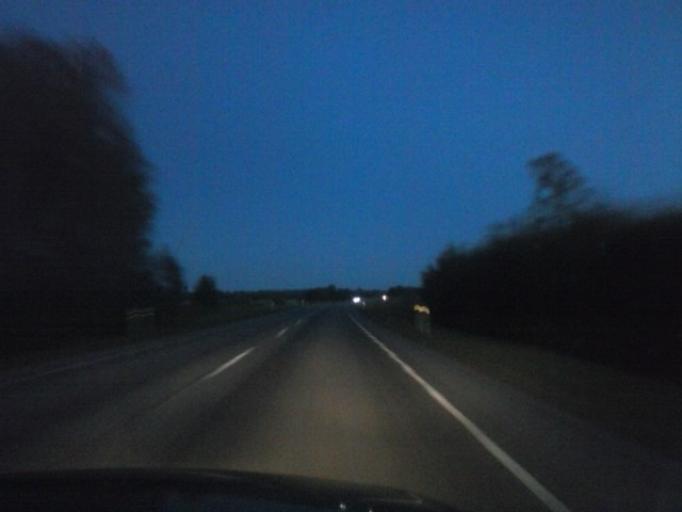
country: EE
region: Viljandimaa
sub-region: Vohma linn
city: Vohma
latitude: 58.7394
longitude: 25.5840
